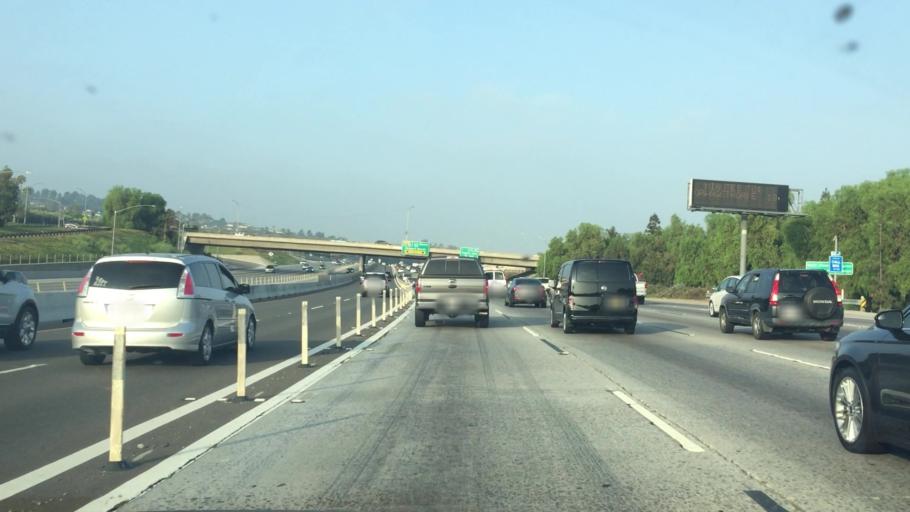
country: US
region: California
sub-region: Orange County
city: Yorba Linda
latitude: 33.8526
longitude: -117.8131
